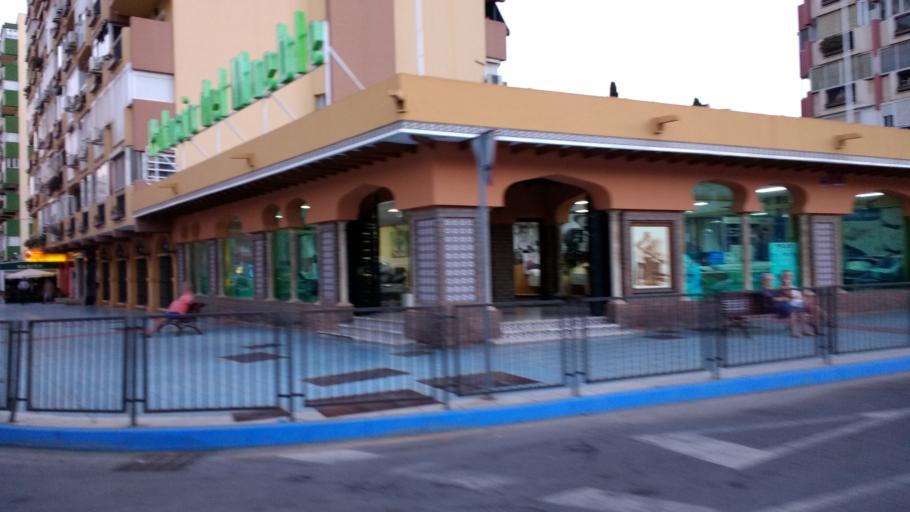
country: ES
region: Andalusia
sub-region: Provincia de Malaga
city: Velez-Malaga
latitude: 36.7385
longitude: -4.0997
